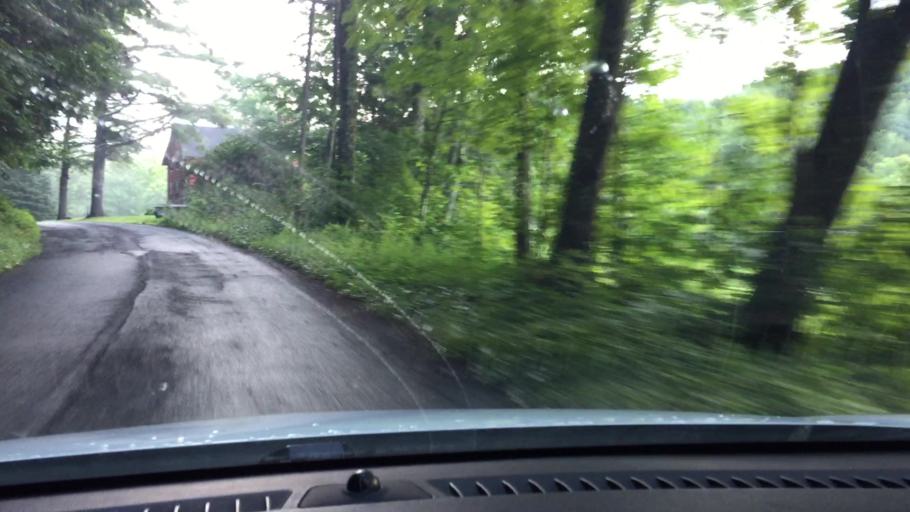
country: US
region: Massachusetts
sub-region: Hampshire County
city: Chesterfield
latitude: 42.3302
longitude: -72.9327
